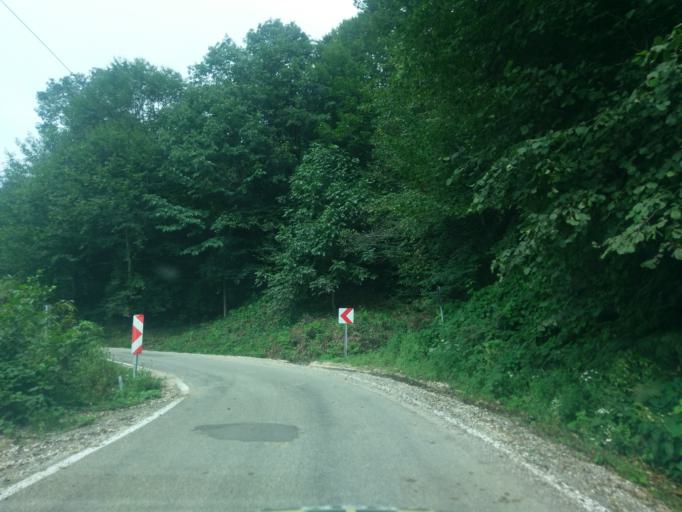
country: TR
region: Ordu
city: Gurgentepe
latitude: 40.8499
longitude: 37.6543
